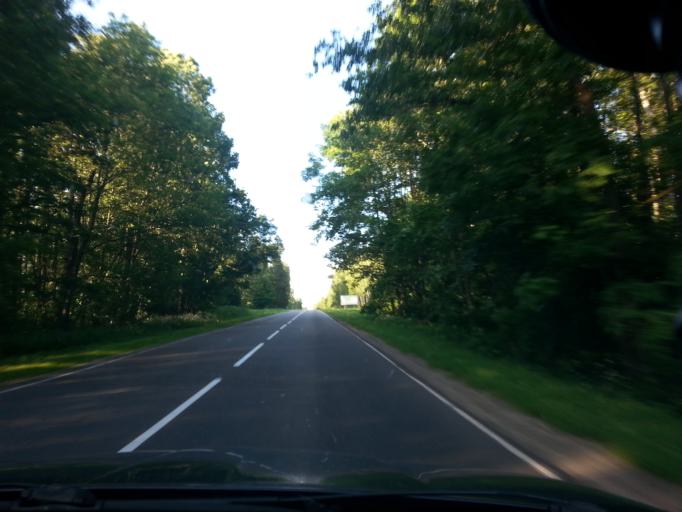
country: BY
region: Minsk
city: Svir
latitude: 54.8993
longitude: 26.4108
